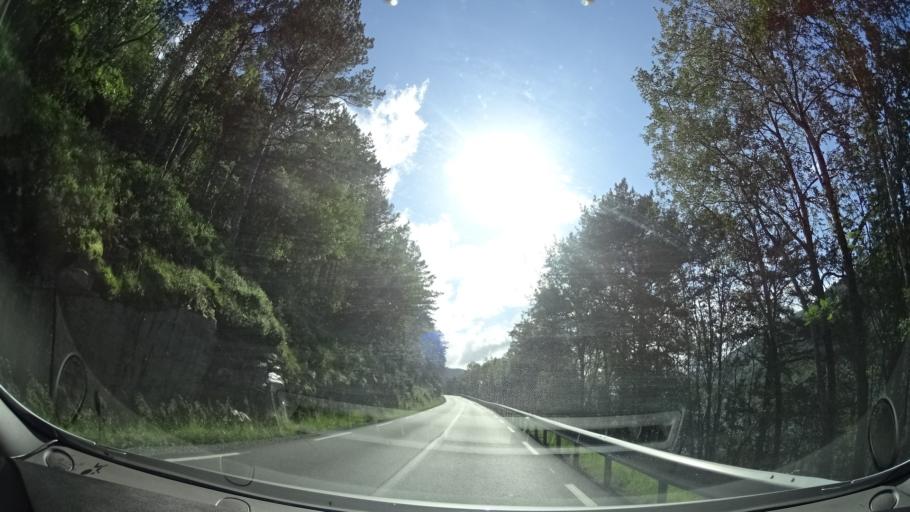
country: NO
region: Sor-Trondelag
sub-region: Hemne
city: Kyrksaeterora
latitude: 63.2003
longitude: 8.9671
